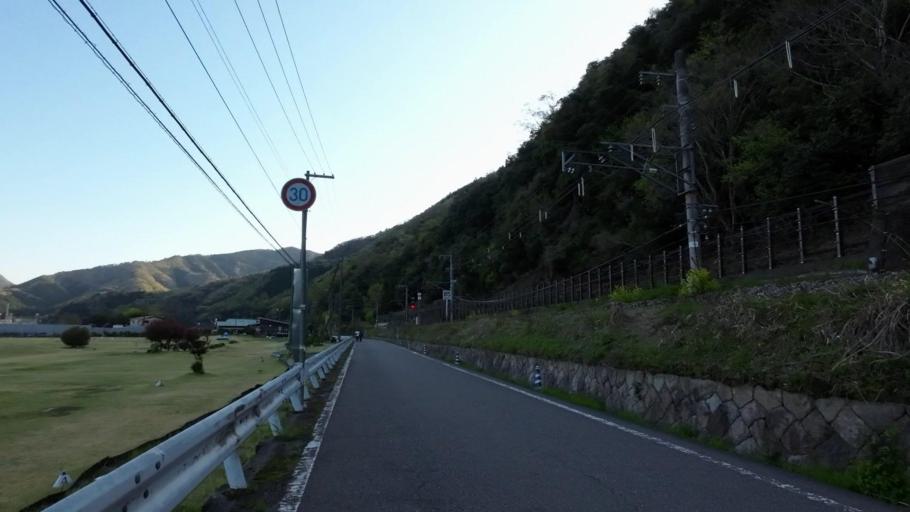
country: JP
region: Hyogo
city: Toyooka
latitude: 35.3788
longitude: 134.8117
